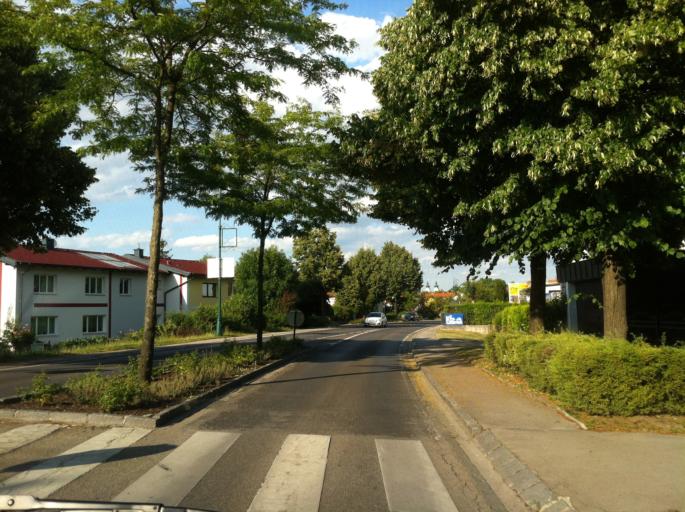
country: AT
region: Lower Austria
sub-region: Politischer Bezirk Tulln
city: Tulln
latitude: 48.3279
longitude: 16.0438
